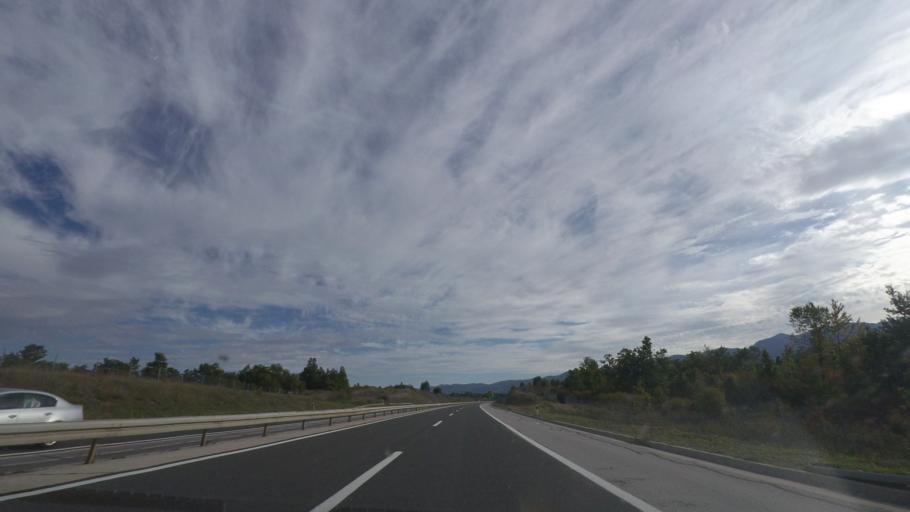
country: HR
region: Zadarska
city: Obrovac
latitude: 44.4169
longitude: 15.6381
